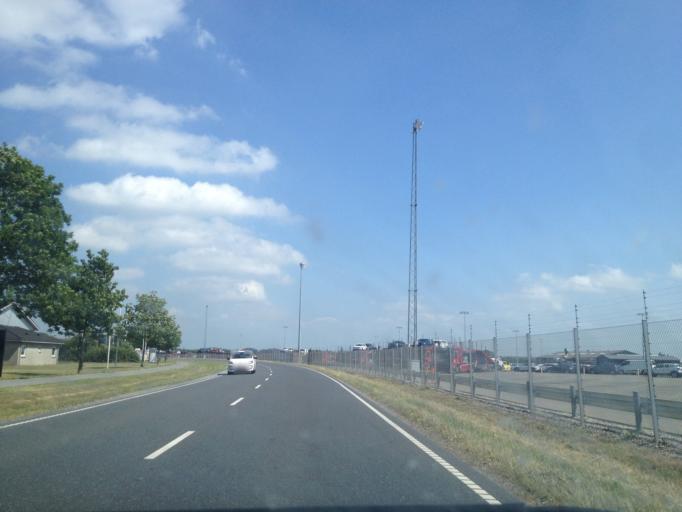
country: DK
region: South Denmark
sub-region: Kolding Kommune
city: Vamdrup
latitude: 55.4366
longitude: 9.3050
